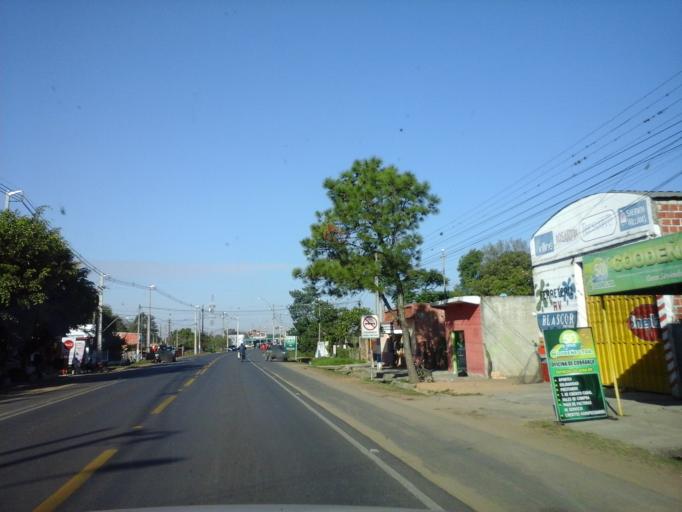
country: PY
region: Neembucu
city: Pilar
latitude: -26.8508
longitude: -58.2948
